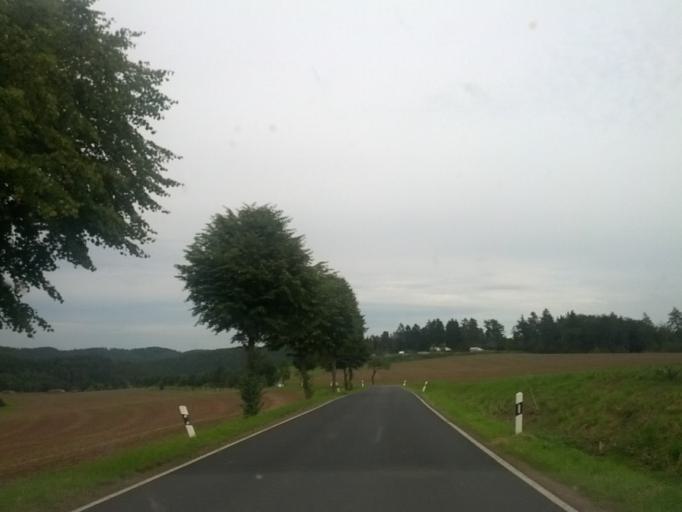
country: DE
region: Thuringia
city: Wolfsburg-Unkeroda
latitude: 50.9160
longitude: 10.2702
